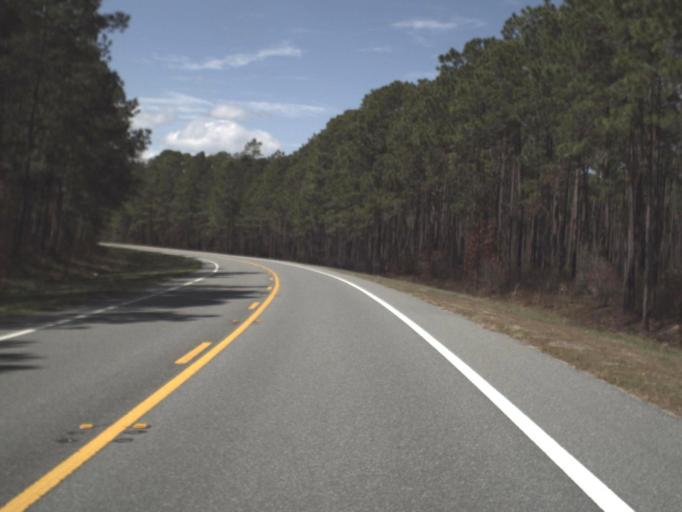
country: US
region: Florida
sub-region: Gadsden County
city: Midway
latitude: 30.3878
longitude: -84.5749
